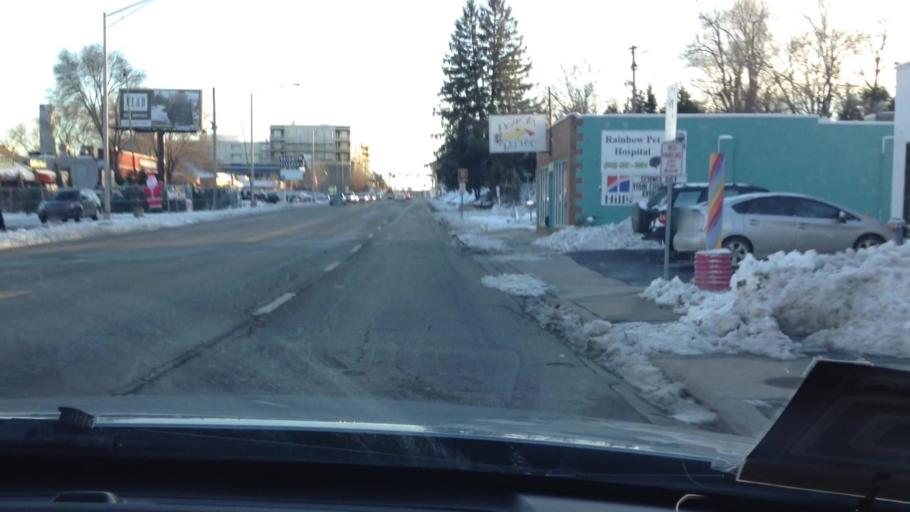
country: US
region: Kansas
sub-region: Johnson County
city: Westwood
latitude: 39.0465
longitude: -94.6120
